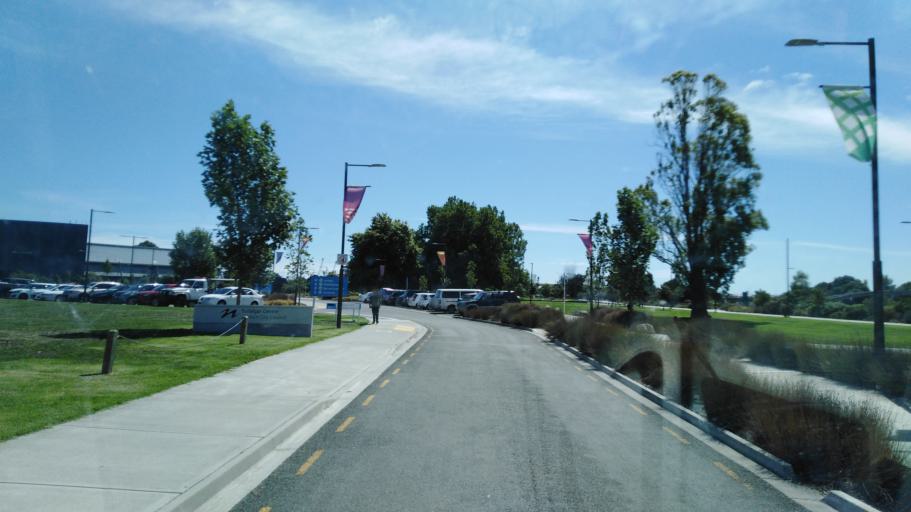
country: NZ
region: Nelson
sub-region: Nelson City
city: Nelson
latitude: -41.2688
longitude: 173.2813
